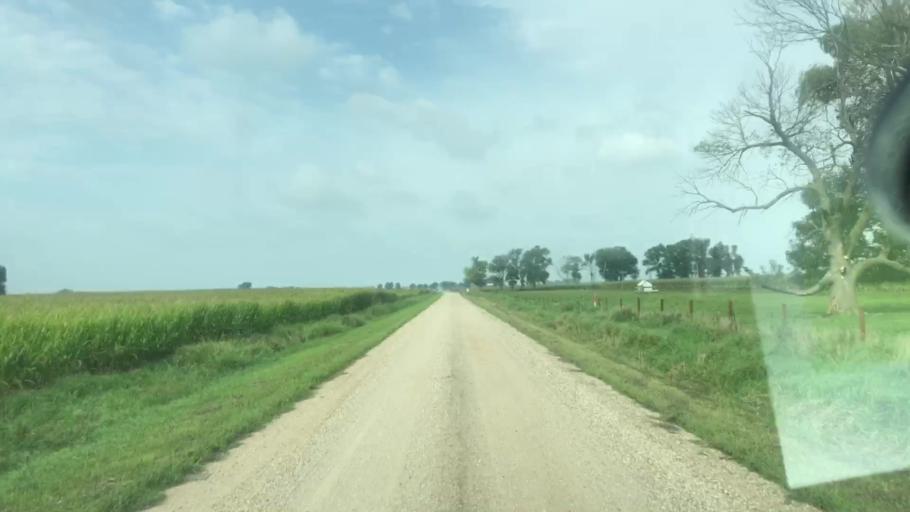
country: US
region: Iowa
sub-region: O'Brien County
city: Sheldon
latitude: 43.2724
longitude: -95.8967
